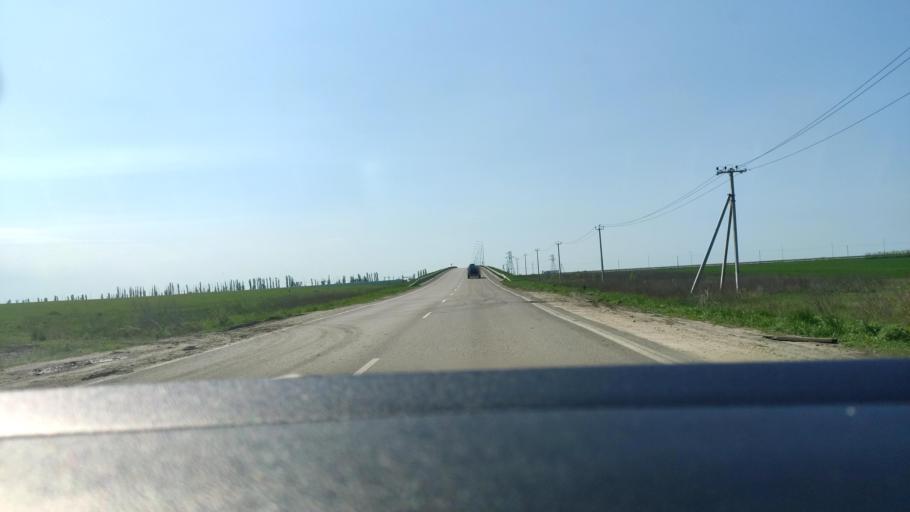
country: RU
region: Voronezj
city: Novaya Usman'
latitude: 51.5957
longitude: 39.3737
